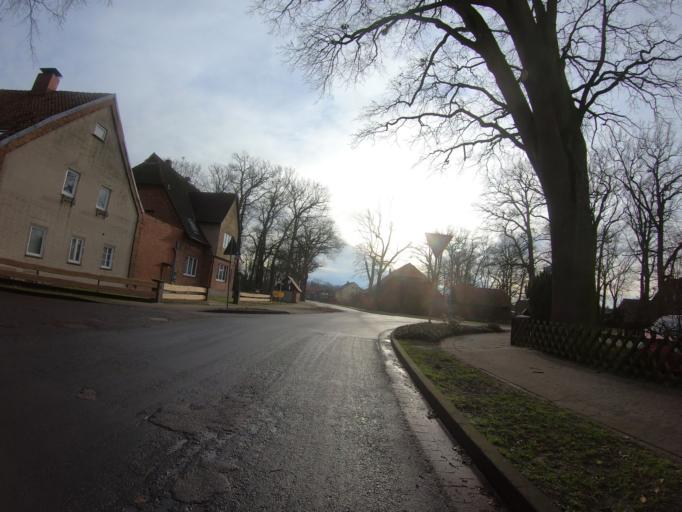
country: DE
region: Lower Saxony
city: Muden
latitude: 52.5016
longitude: 10.4088
